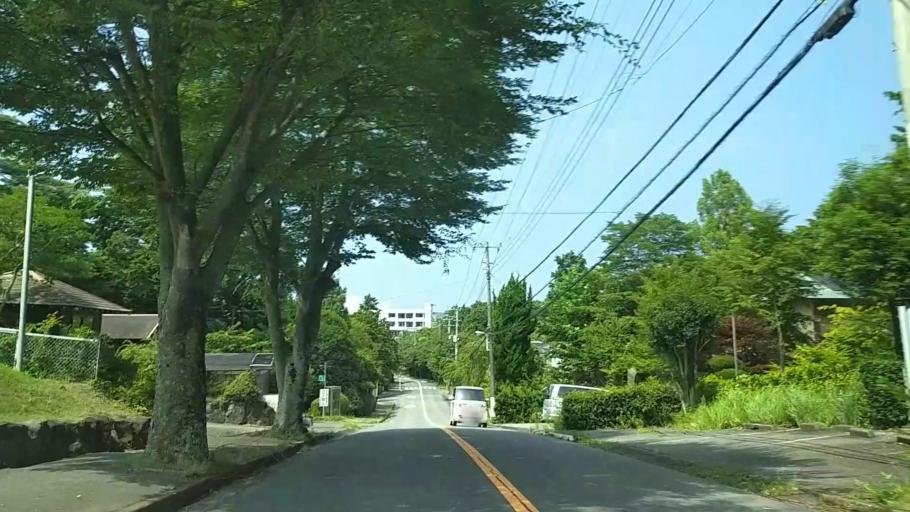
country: JP
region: Shizuoka
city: Ito
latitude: 34.9230
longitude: 139.1063
